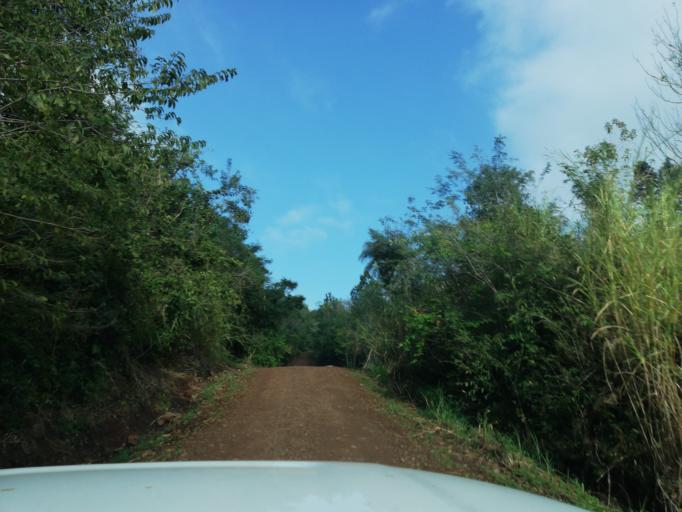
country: AR
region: Misiones
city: Cerro Azul
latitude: -27.5736
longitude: -55.5026
